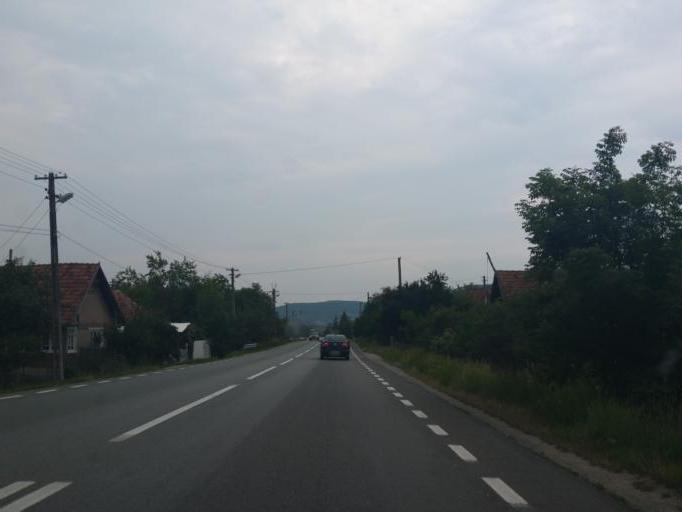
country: RO
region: Salaj
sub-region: Comuna Sanmihaiu Almasului
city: Sanmihaiu Almasului
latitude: 46.9579
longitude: 23.3351
